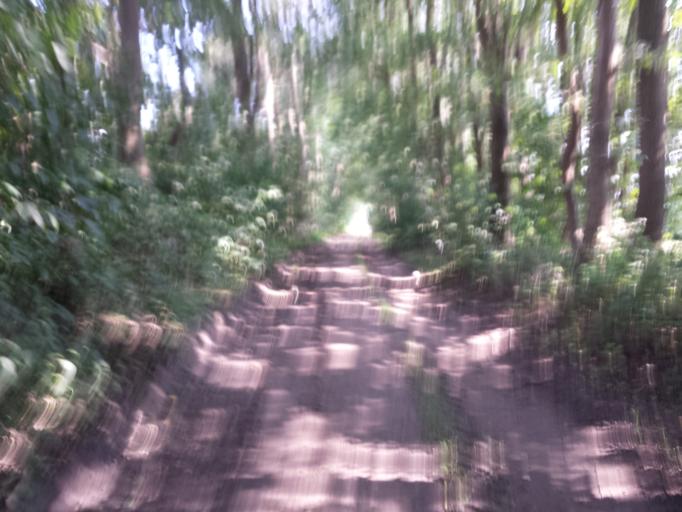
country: DE
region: North Rhine-Westphalia
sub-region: Regierungsbezirk Detmold
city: Guetersloh
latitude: 51.8845
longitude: 8.4137
